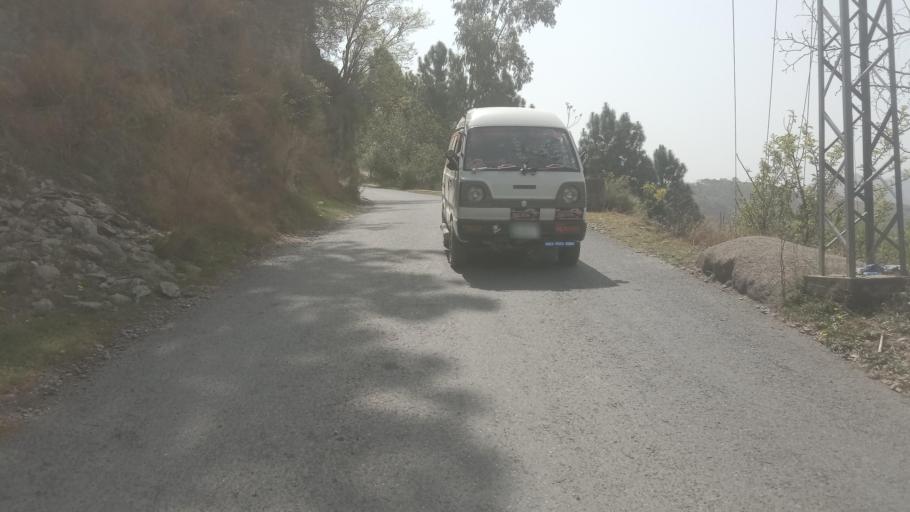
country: PK
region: Khyber Pakhtunkhwa
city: Abbottabad
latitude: 34.1675
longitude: 73.2843
